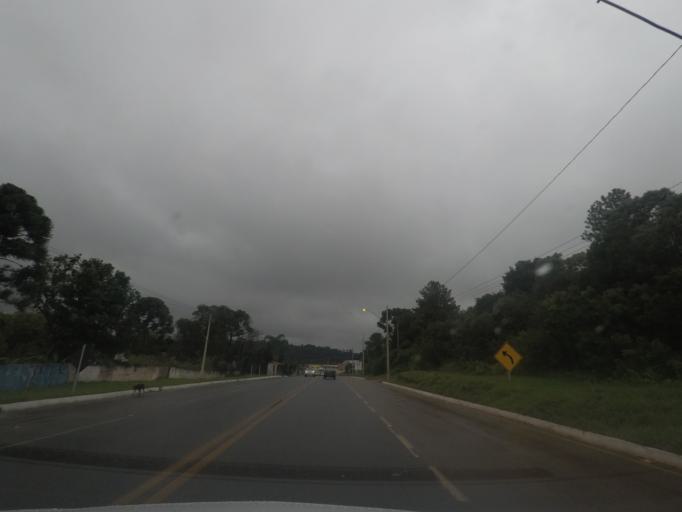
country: BR
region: Parana
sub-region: Colombo
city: Colombo
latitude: -25.3424
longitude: -49.1584
